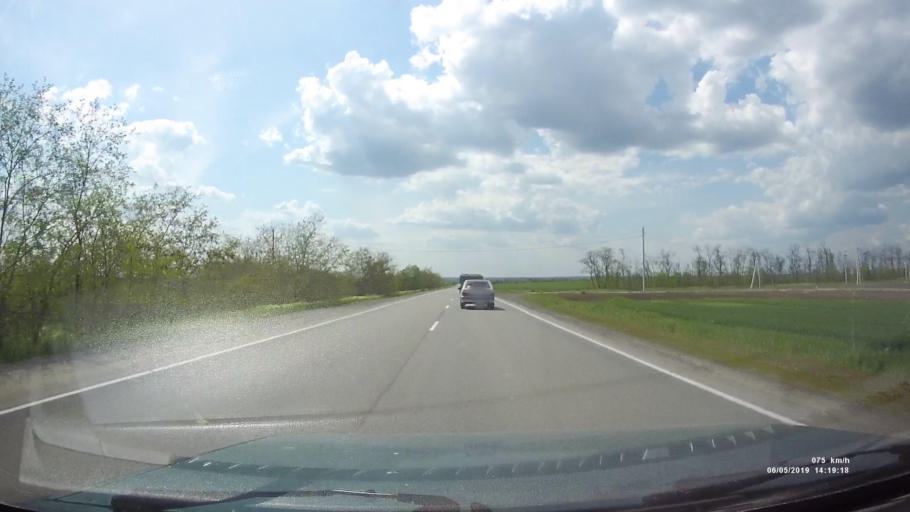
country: RU
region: Rostov
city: Kamenolomni
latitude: 47.6329
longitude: 40.2347
